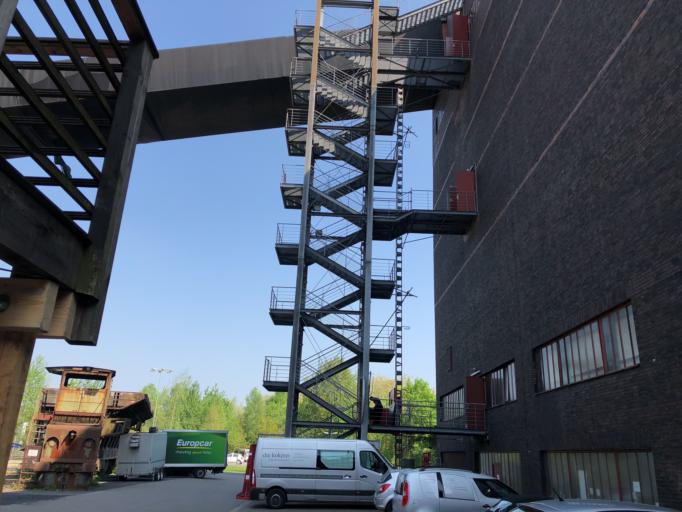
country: DE
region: North Rhine-Westphalia
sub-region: Regierungsbezirk Dusseldorf
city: Essen
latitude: 51.4905
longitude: 7.0387
